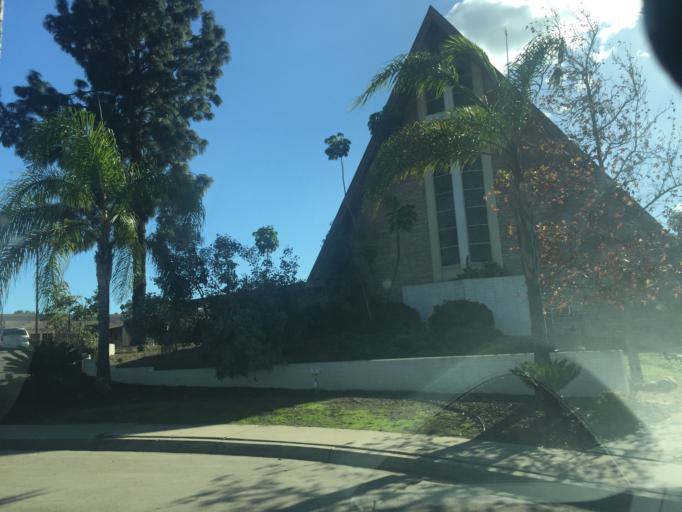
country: US
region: California
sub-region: San Diego County
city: La Mesa
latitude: 32.7875
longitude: -117.0837
